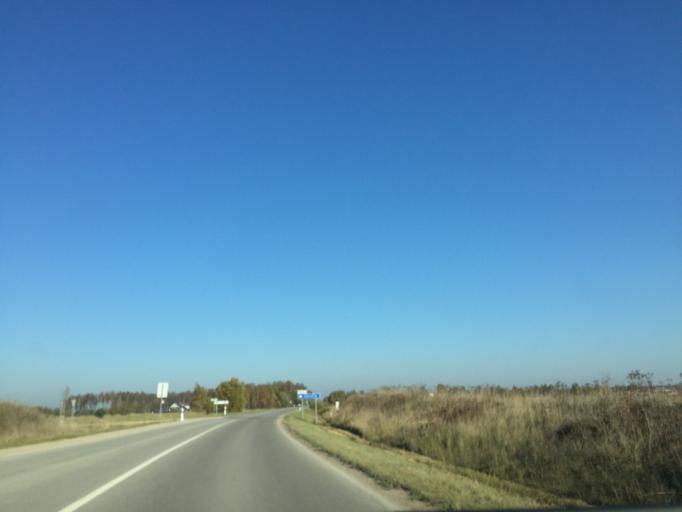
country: LT
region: Klaipedos apskritis
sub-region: Klaipeda
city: Klaipeda
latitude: 55.7714
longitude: 21.1968
